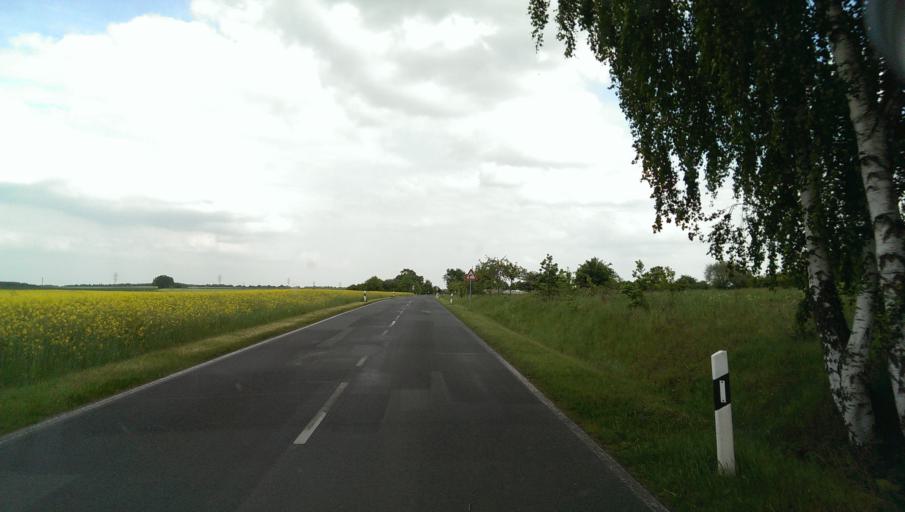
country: DE
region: Brandenburg
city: Belzig
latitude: 52.1075
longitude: 12.5390
